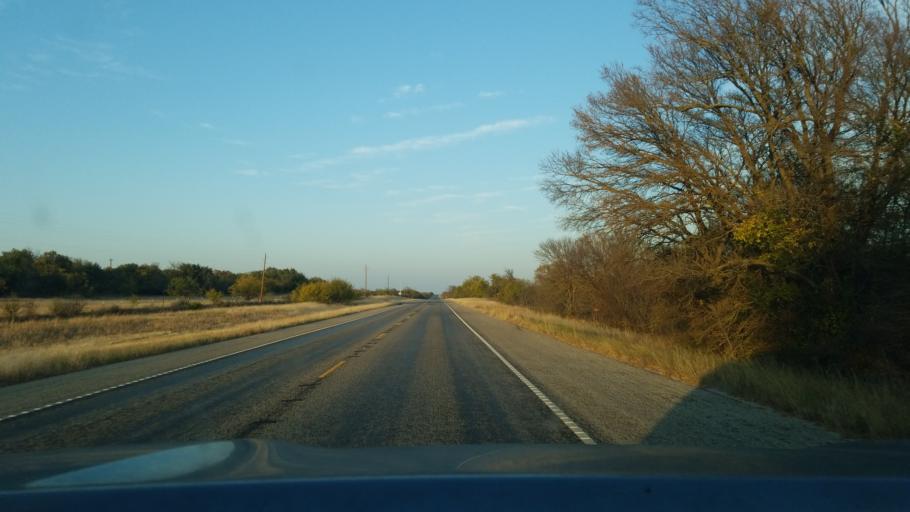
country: US
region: Texas
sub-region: Eastland County
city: Cisco
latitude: 32.4155
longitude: -98.9420
